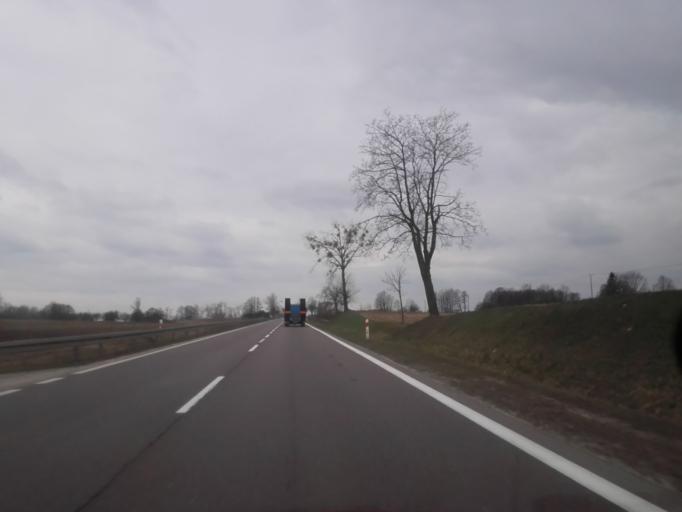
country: PL
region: Podlasie
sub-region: Powiat augustowski
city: Augustow
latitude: 53.8010
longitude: 22.8879
